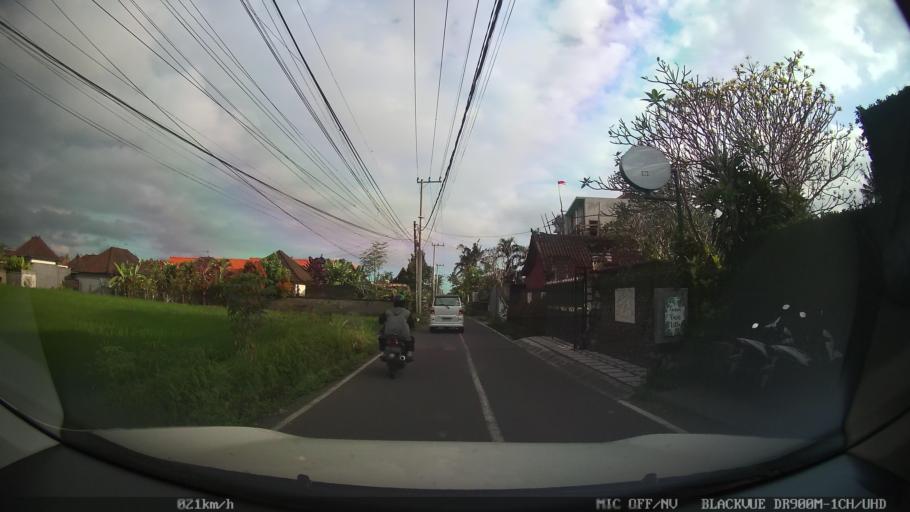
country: ID
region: Bali
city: Banjar Pande
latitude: -8.5157
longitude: 115.2501
